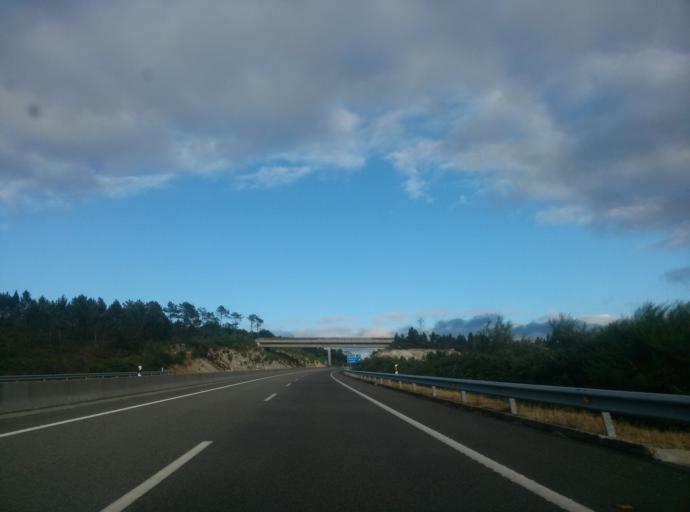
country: ES
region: Galicia
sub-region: Provincia de Lugo
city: Vilalba
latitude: 43.3587
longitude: -7.7564
